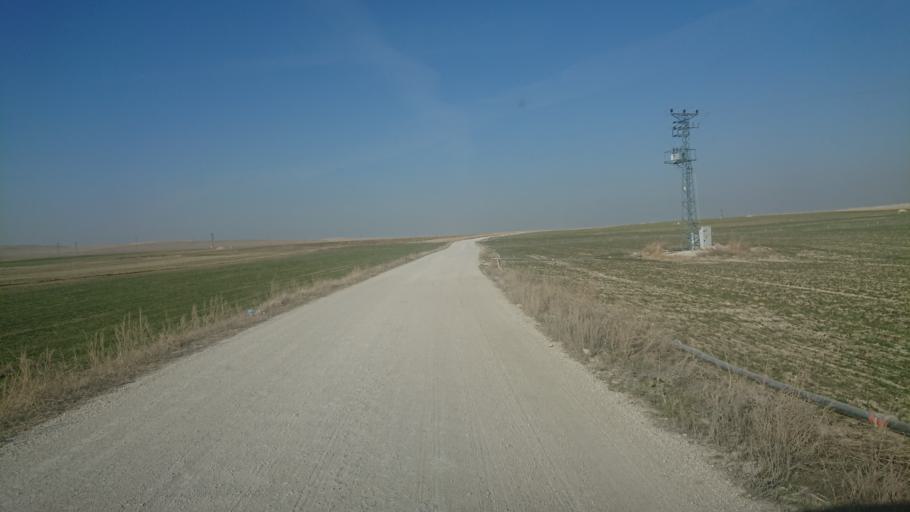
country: TR
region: Aksaray
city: Sultanhani
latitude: 38.0399
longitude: 33.6059
